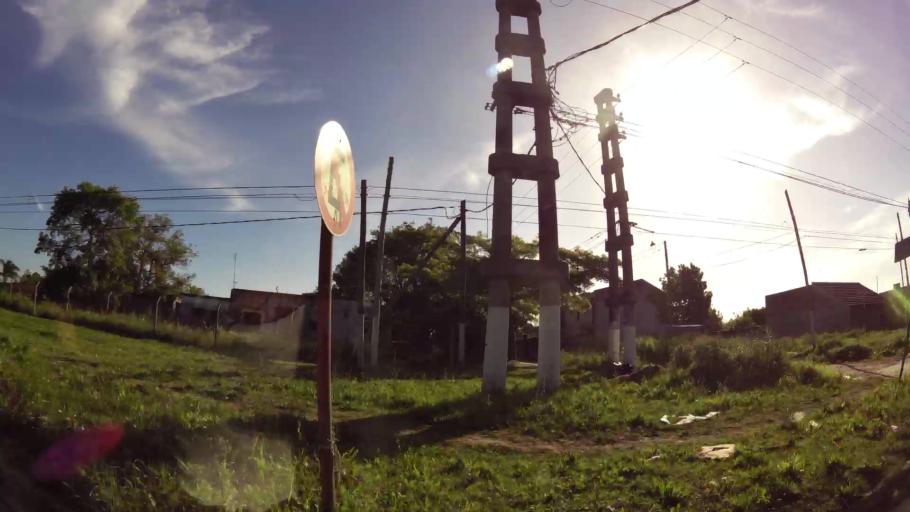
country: AR
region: Buenos Aires
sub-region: Partido de Quilmes
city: Quilmes
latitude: -34.7912
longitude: -58.2169
